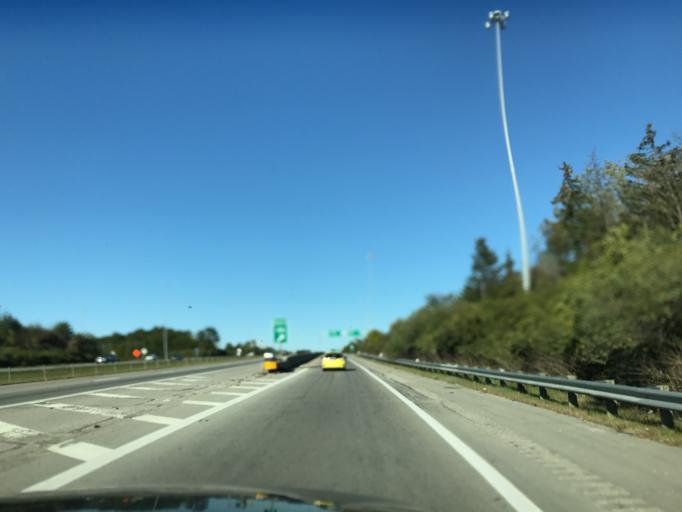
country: US
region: Ohio
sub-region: Franklin County
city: Groveport
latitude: 39.8981
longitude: -82.9020
